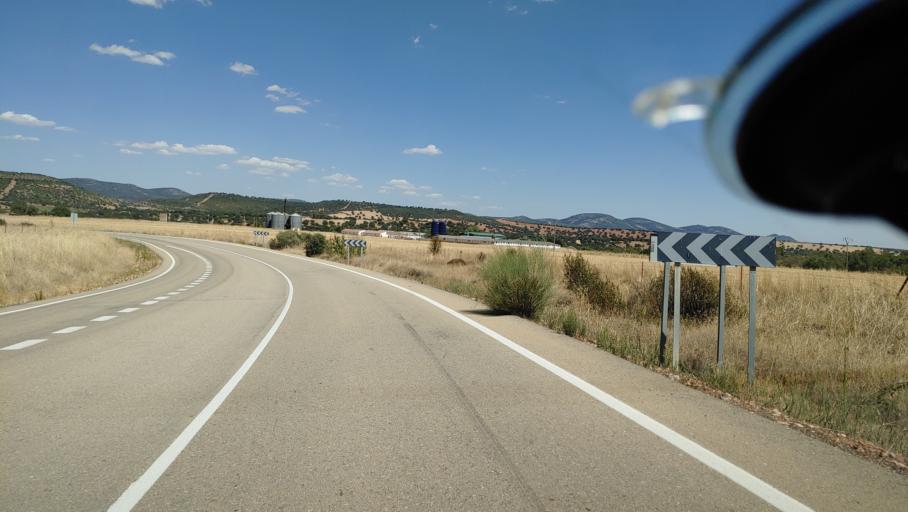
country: ES
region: Castille-La Mancha
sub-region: Provincia de Ciudad Real
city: Saceruela
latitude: 39.0116
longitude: -4.4972
